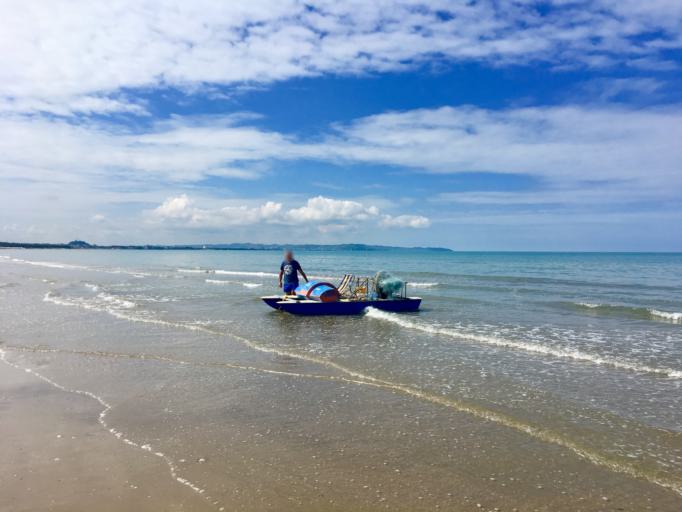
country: AL
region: Tirane
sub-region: Rrethi i Kavajes
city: Golem
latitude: 41.2790
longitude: 19.5128
